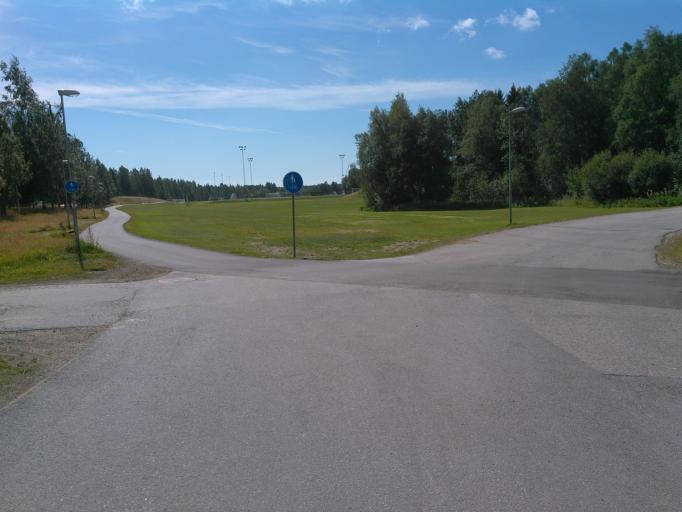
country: SE
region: Vaesterbotten
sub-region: Umea Kommun
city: Ersmark
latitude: 63.8432
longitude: 20.3145
